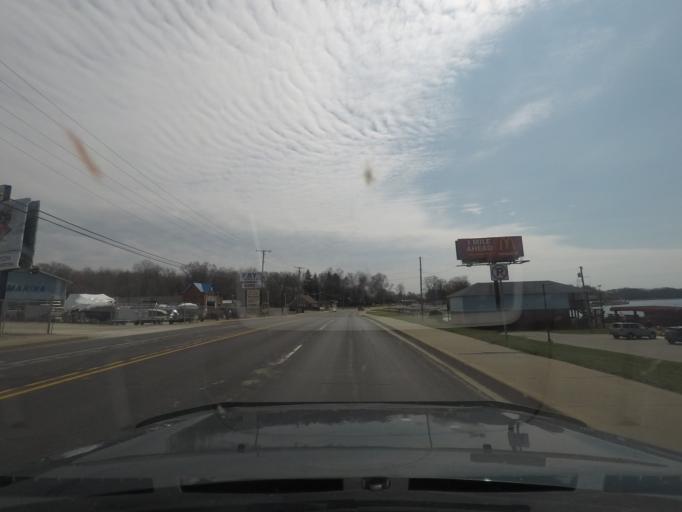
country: US
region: Indiana
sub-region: LaPorte County
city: LaPorte
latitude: 41.6292
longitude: -86.7381
